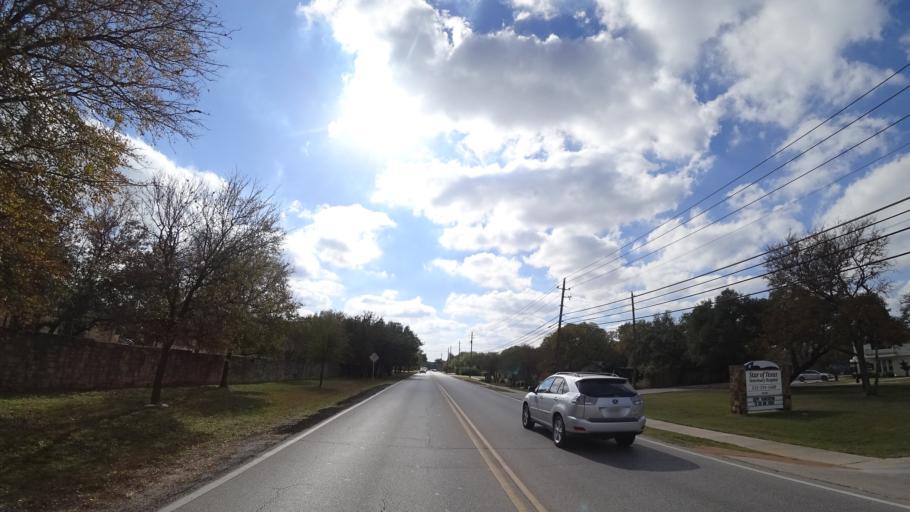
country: US
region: Texas
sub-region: Travis County
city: Shady Hollow
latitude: 30.1745
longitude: -97.8555
